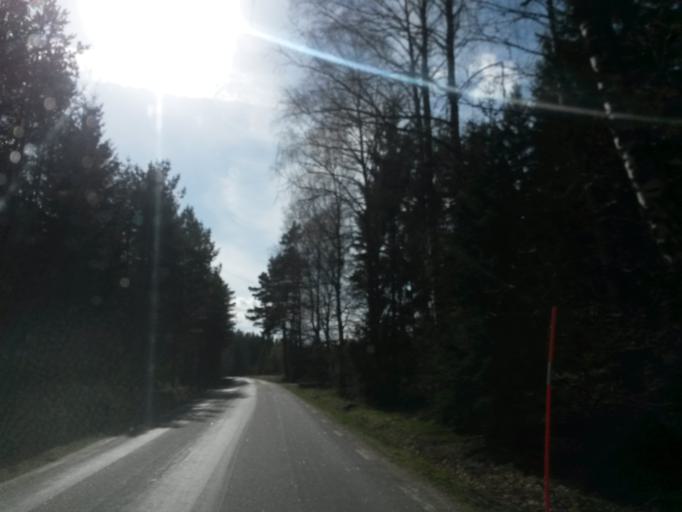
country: SE
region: Vaestra Goetaland
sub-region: Vargarda Kommun
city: Jonstorp
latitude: 57.9482
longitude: 12.7119
